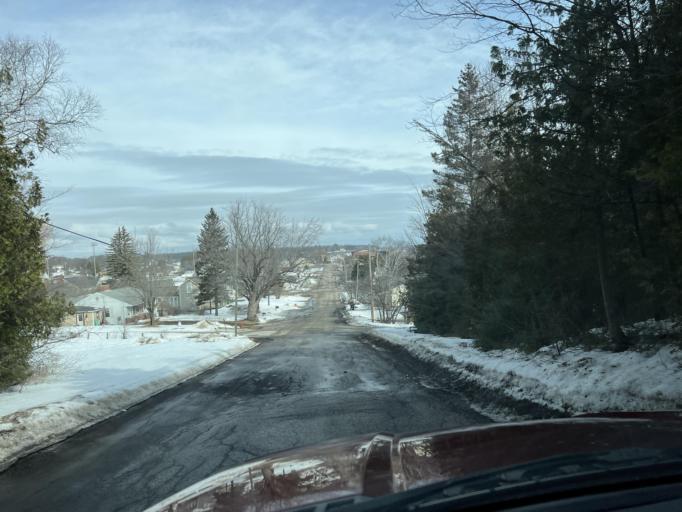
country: US
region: Michigan
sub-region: Mackinac County
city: Saint Ignace
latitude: 45.8628
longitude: -84.7240
